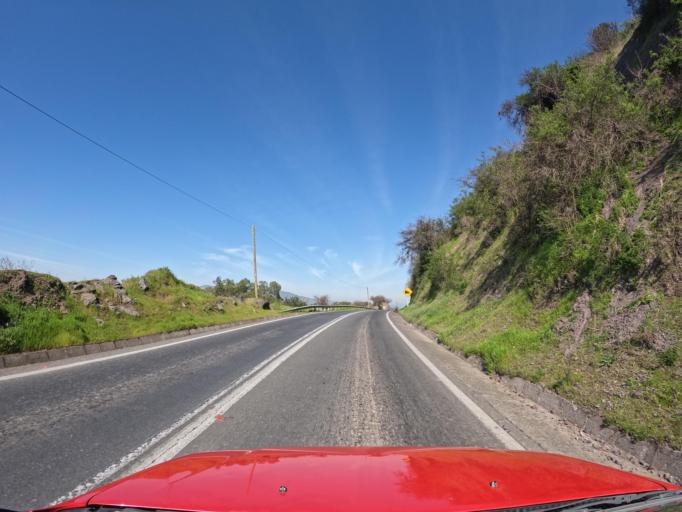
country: CL
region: Maule
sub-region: Provincia de Curico
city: Rauco
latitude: -34.9752
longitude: -71.3831
